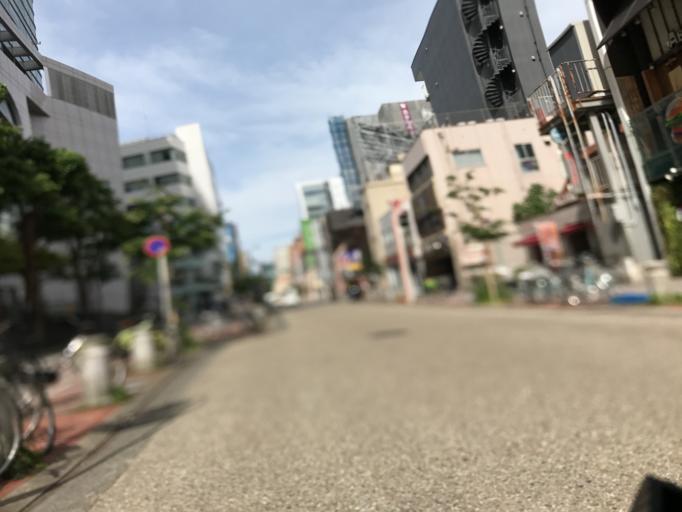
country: JP
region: Aichi
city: Nagoya-shi
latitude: 35.1659
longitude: 136.9057
